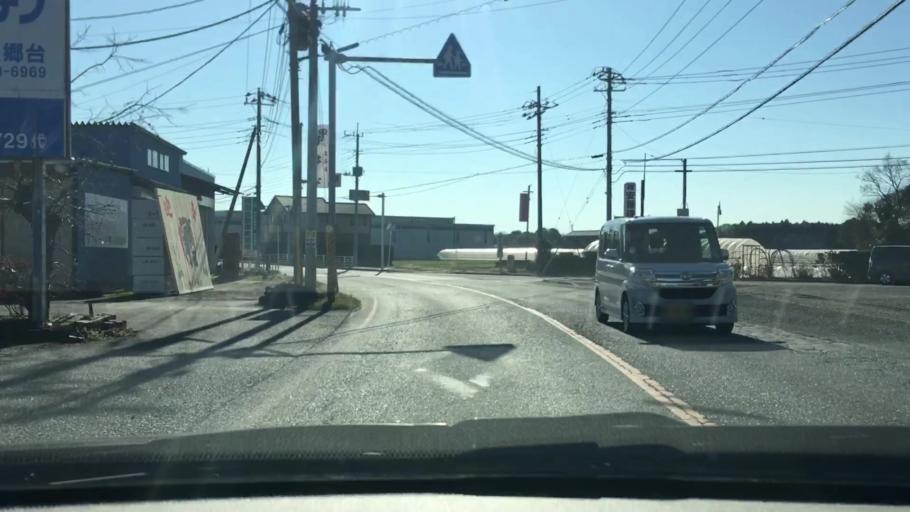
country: JP
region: Chiba
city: Shisui
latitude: 35.7071
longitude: 140.3148
